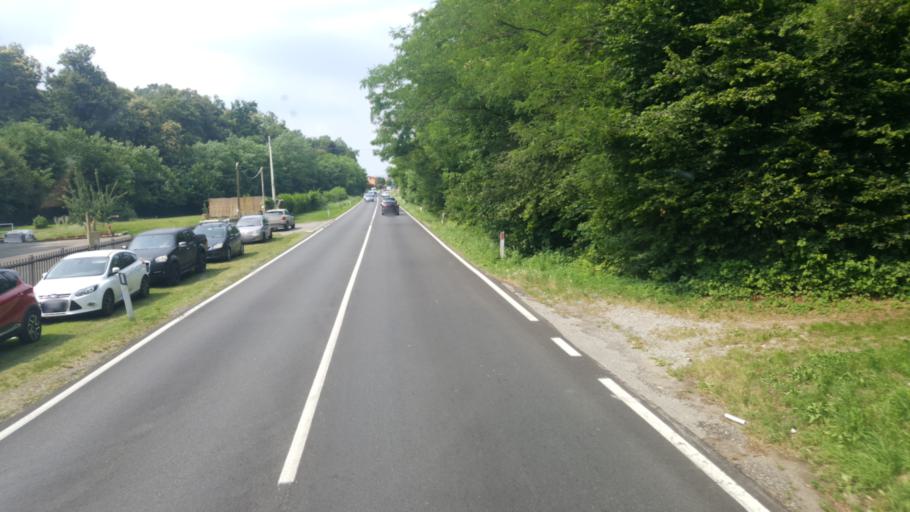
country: IT
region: Lombardy
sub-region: Provincia di Como
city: Beregazzo
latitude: 45.7630
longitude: 8.9620
